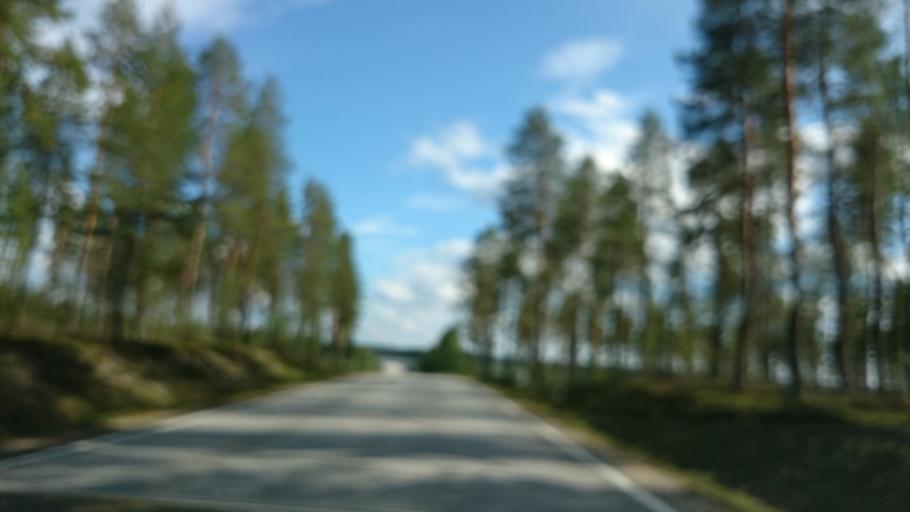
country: FI
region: Kainuu
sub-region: Kehys-Kainuu
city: Suomussalmi
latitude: 64.7662
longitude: 29.3686
